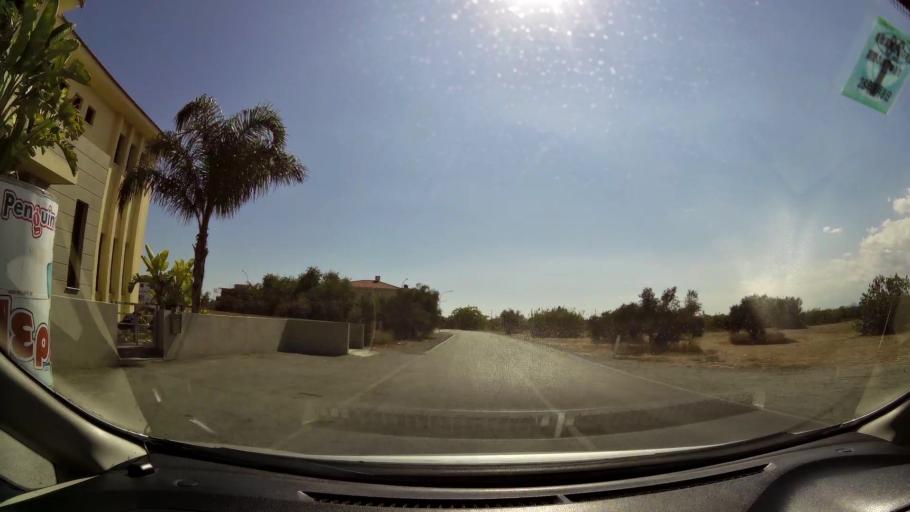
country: CY
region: Larnaka
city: Livadia
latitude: 34.9550
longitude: 33.6218
